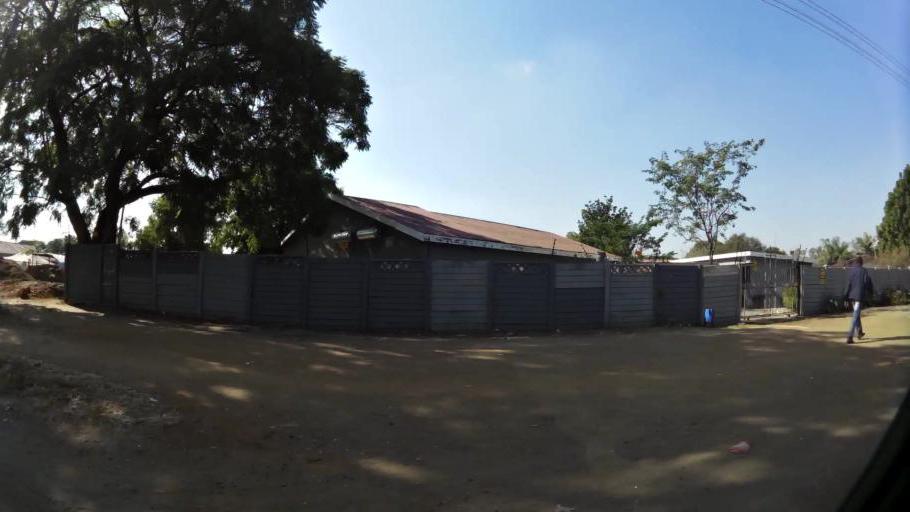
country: ZA
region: North-West
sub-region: Bojanala Platinum District Municipality
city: Rustenburg
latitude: -25.6600
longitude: 27.2321
